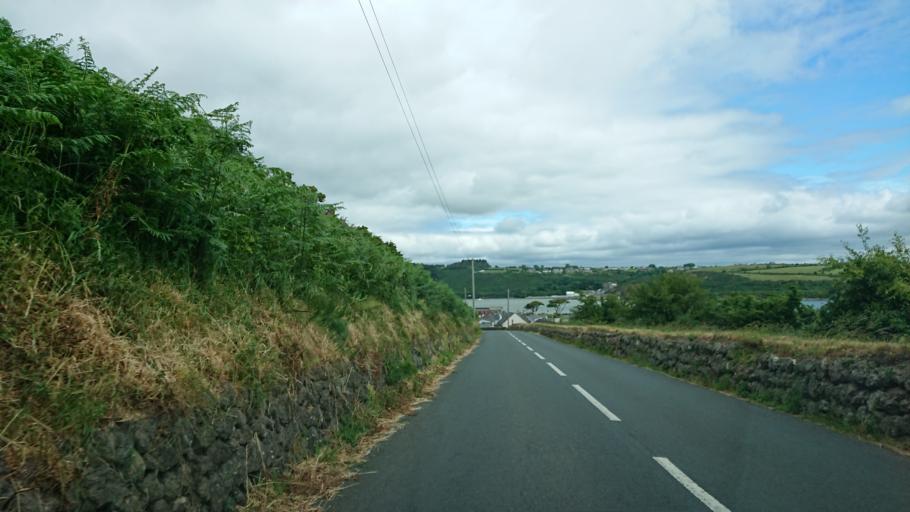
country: IE
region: Munster
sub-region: Waterford
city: Dunmore East
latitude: 52.2356
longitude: -6.9720
